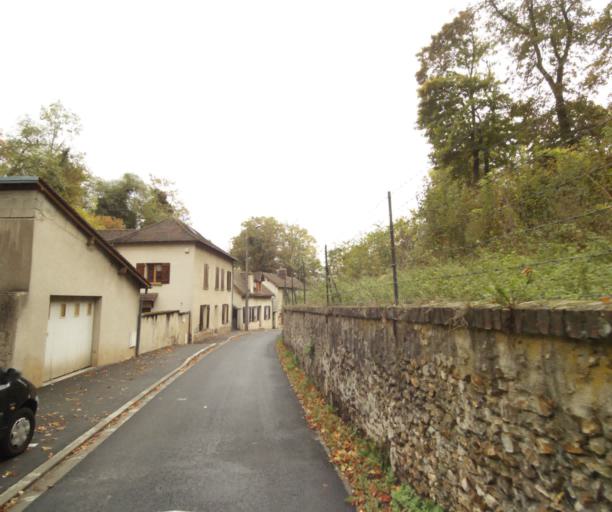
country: FR
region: Centre
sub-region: Departement d'Eure-et-Loir
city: Dreux
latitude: 48.7406
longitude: 1.3661
